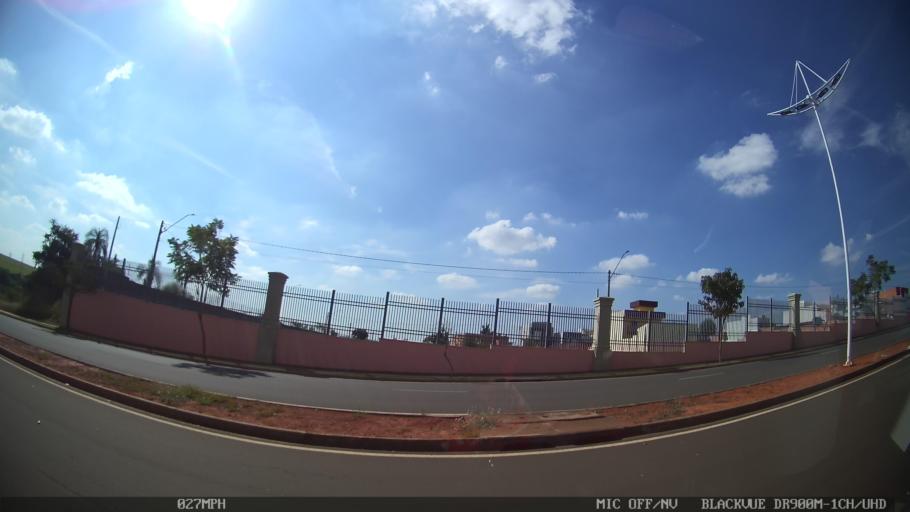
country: BR
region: Sao Paulo
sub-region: Hortolandia
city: Hortolandia
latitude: -22.8690
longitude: -47.2372
